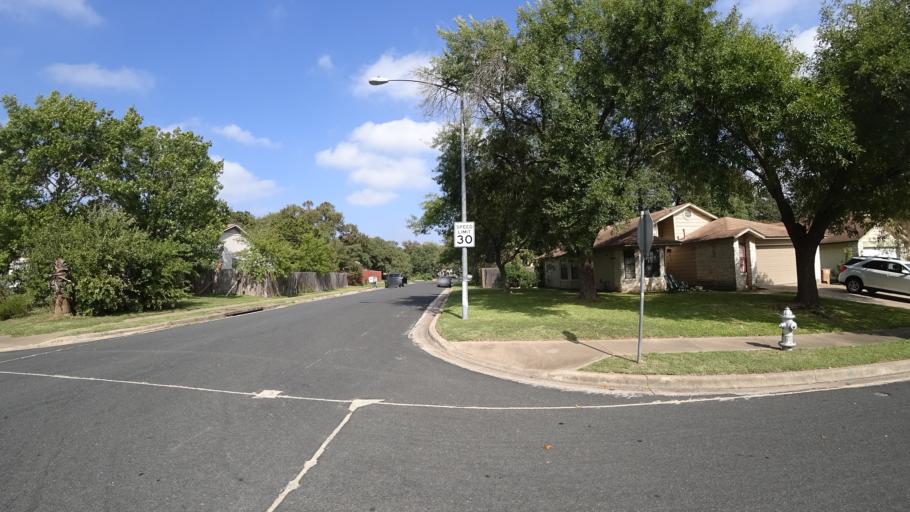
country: US
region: Texas
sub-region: Travis County
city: Shady Hollow
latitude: 30.2005
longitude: -97.8258
